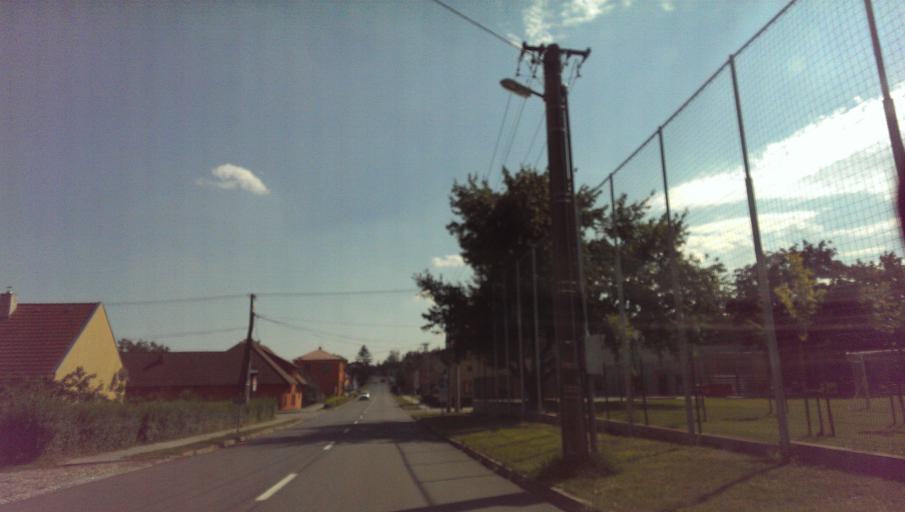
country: CZ
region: Zlin
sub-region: Okres Zlin
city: Otrokovice
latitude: 49.2564
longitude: 17.5435
